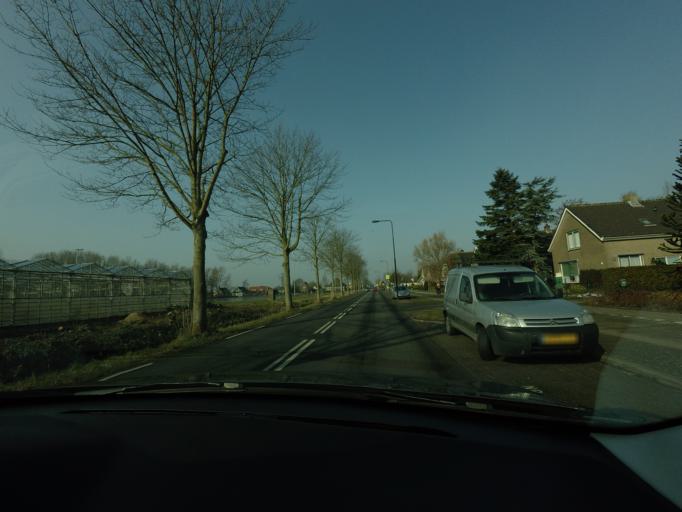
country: NL
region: North Holland
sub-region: Gemeente Heerhugowaard
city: Heerhugowaard
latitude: 52.6497
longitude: 4.8473
